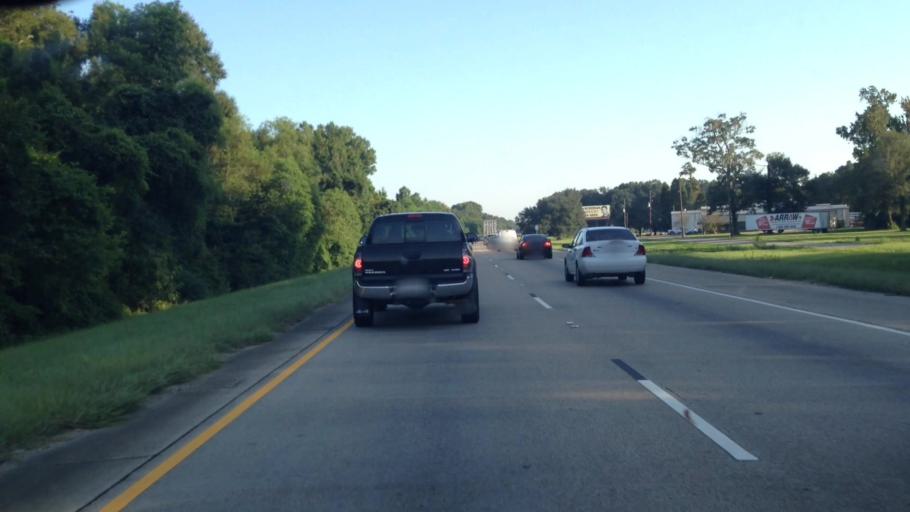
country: US
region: Louisiana
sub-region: Ascension Parish
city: Prairieville
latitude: 30.2769
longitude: -90.9878
